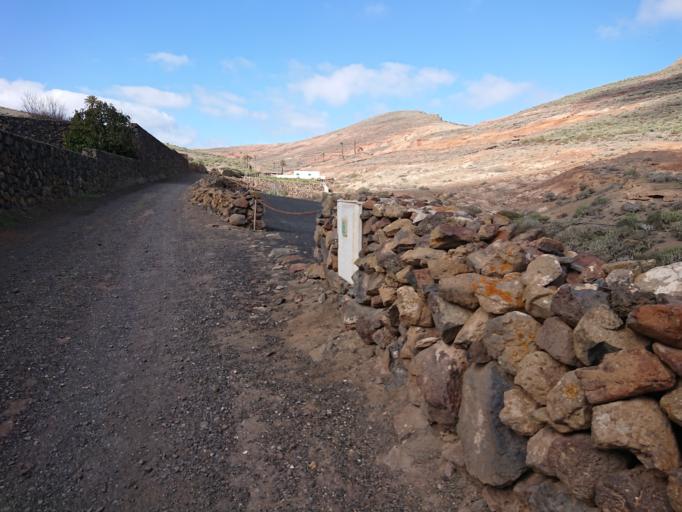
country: ES
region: Canary Islands
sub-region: Provincia de Las Palmas
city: Haria
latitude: 29.1442
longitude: -13.5095
